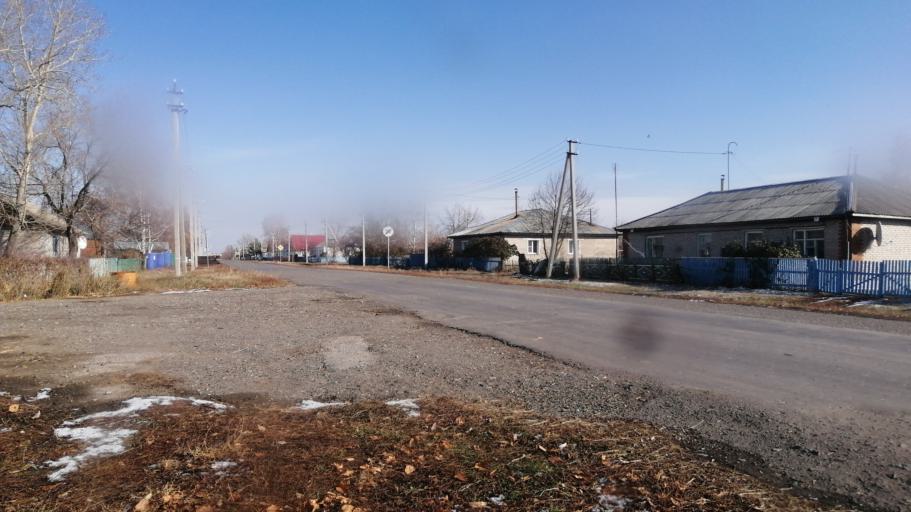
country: RU
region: Novosibirsk
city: Krasnozerskoye
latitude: 53.9558
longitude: 78.8962
